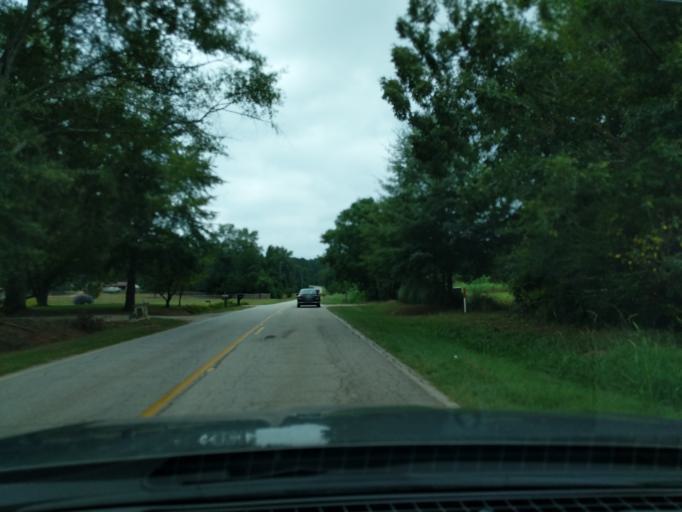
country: US
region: Georgia
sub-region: Columbia County
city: Appling
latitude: 33.6174
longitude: -82.3999
